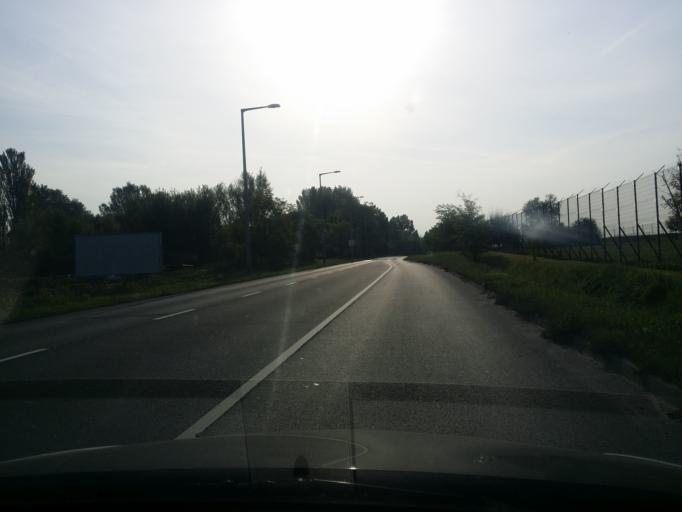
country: HU
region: Budapest
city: Budapest XV. keruelet
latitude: 47.5810
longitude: 19.1392
